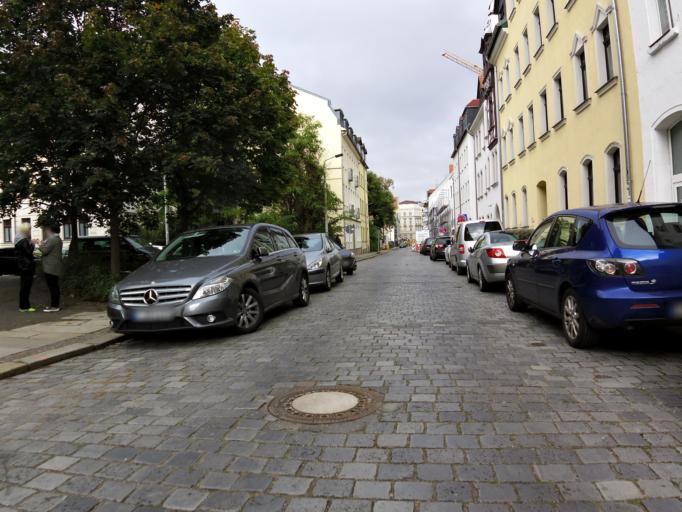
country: DE
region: Saxony
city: Leipzig
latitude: 51.3369
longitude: 12.4009
